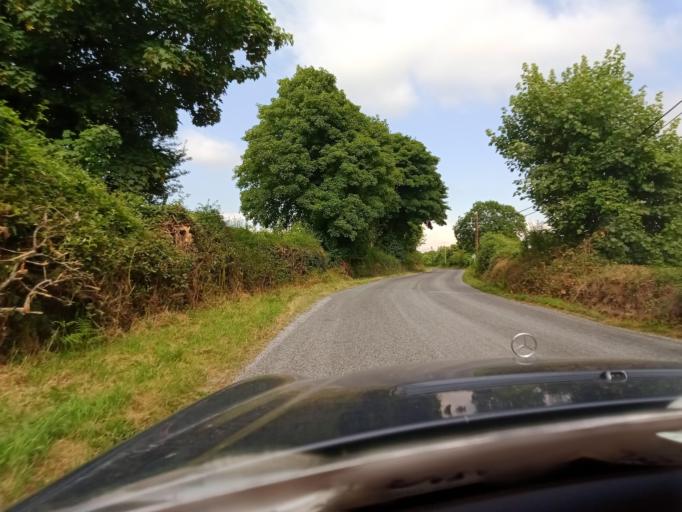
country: IE
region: Leinster
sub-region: Kilkenny
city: Piltown
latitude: 52.4238
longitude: -7.3722
